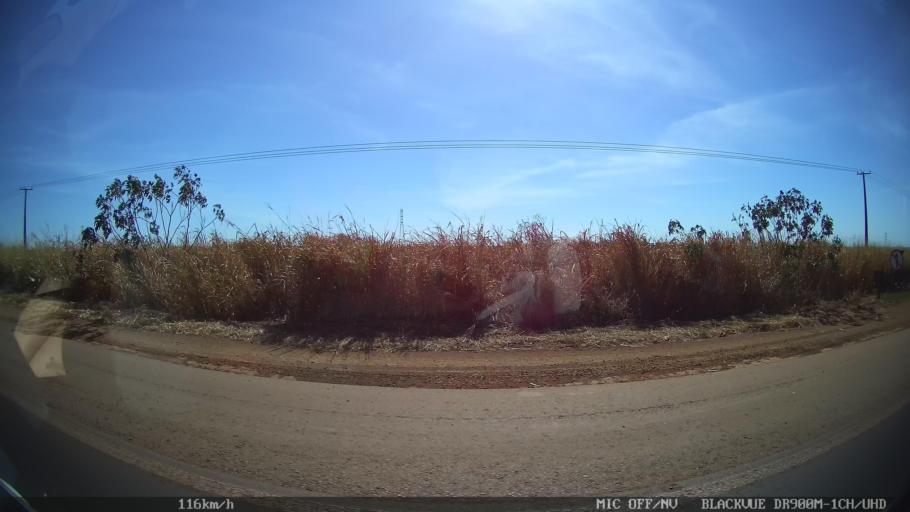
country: BR
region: Sao Paulo
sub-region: Barretos
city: Barretos
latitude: -20.4774
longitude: -48.4978
